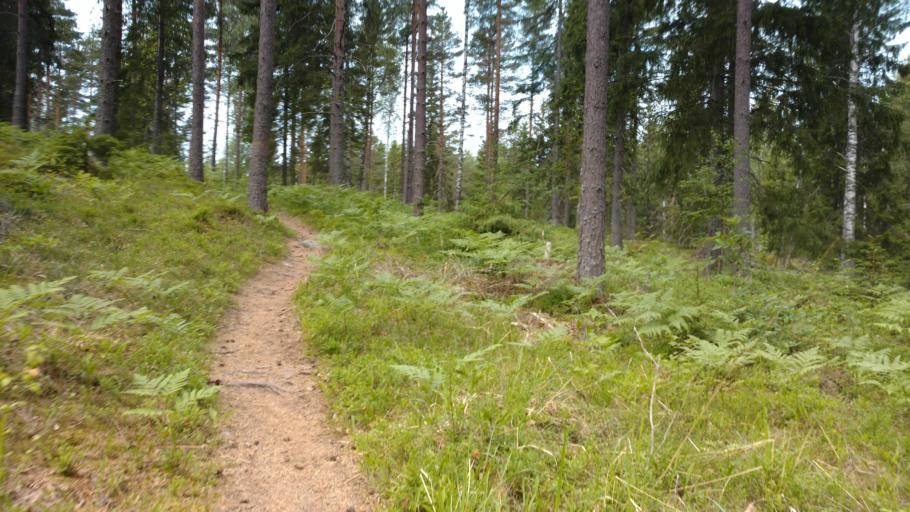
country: FI
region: Uusimaa
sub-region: Raaseporin
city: Pohja
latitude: 60.1187
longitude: 23.5549
